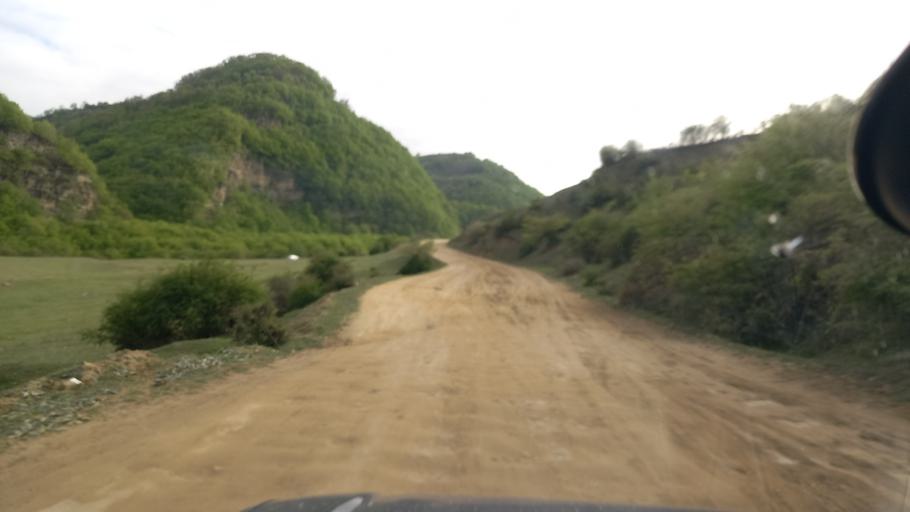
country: RU
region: Dagestan
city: Khuchni
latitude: 41.9635
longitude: 47.8702
